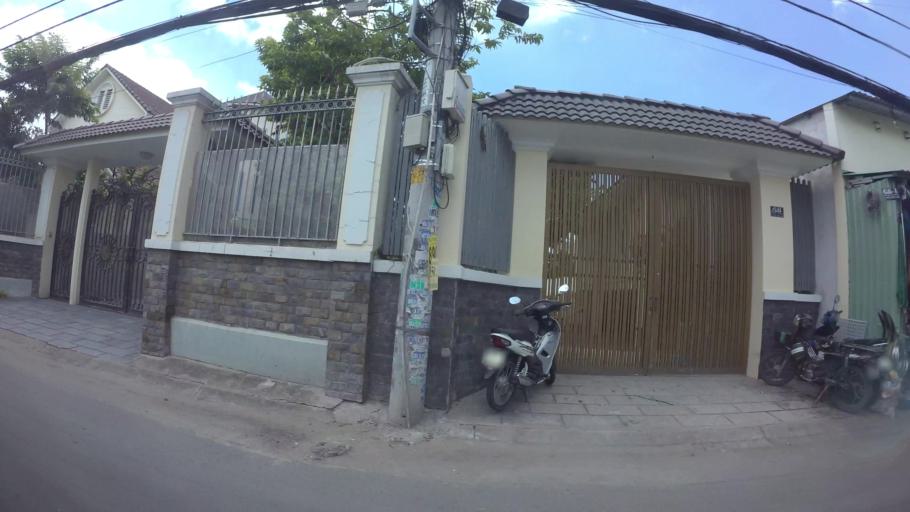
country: VN
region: Ho Chi Minh City
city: Quan Chin
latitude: 10.8237
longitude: 106.7611
